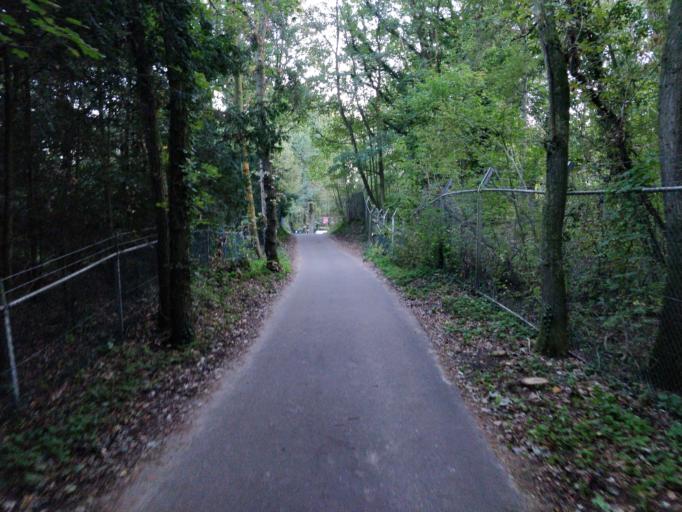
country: NL
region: North Holland
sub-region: Gemeente Zandvoort
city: Zandvoort
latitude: 52.3603
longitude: 4.5709
